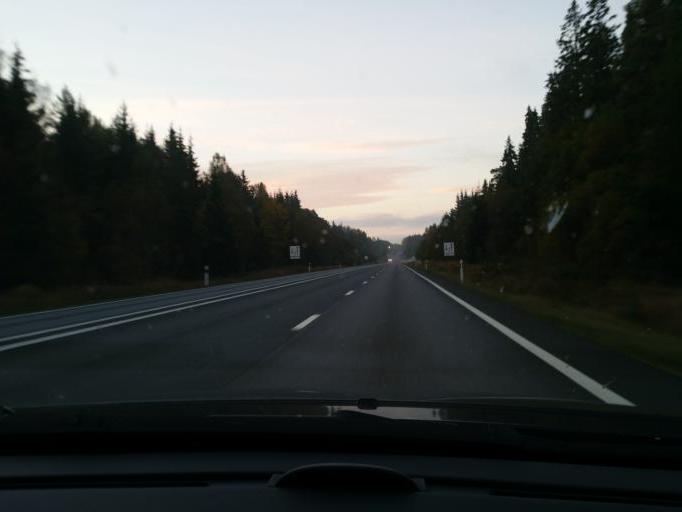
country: SE
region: Kronoberg
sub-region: Vaxjo Kommun
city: Lammhult
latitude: 57.0988
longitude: 14.6382
